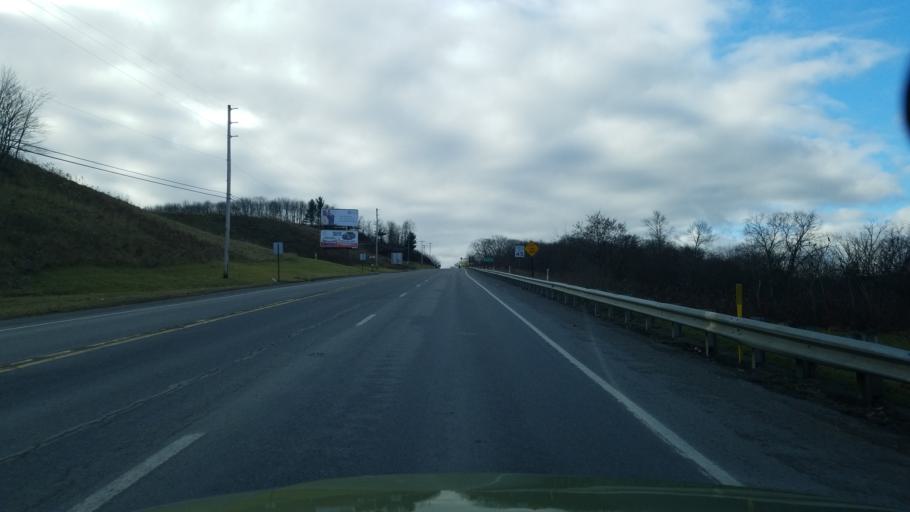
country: US
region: Pennsylvania
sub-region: Jefferson County
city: Punxsutawney
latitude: 40.9337
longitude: -78.9791
